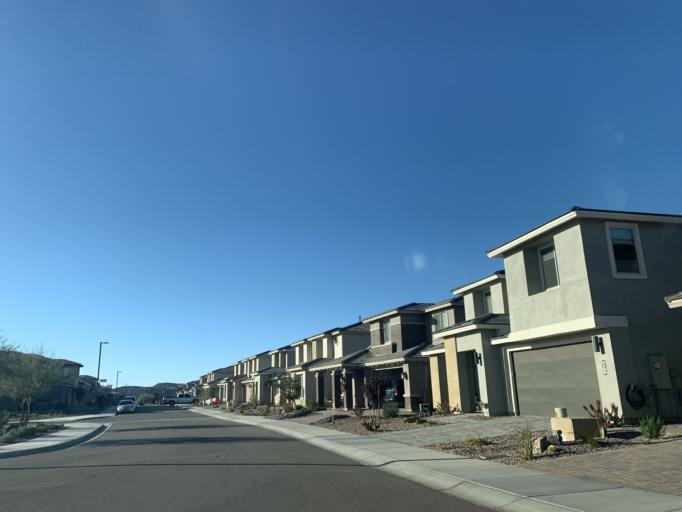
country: US
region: Arizona
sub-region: Maricopa County
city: Cave Creek
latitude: 33.6861
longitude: -112.0164
